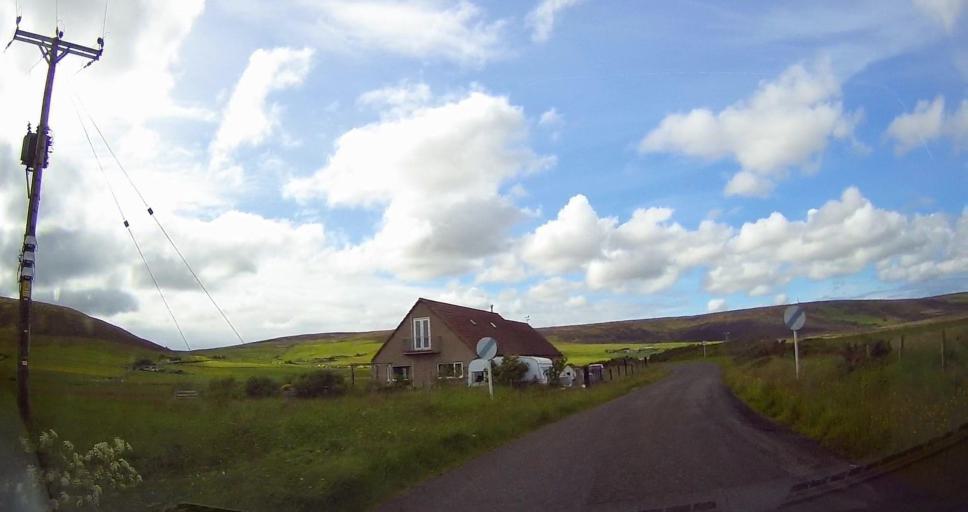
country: GB
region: Scotland
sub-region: Orkney Islands
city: Orkney
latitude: 59.0480
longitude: -3.0835
